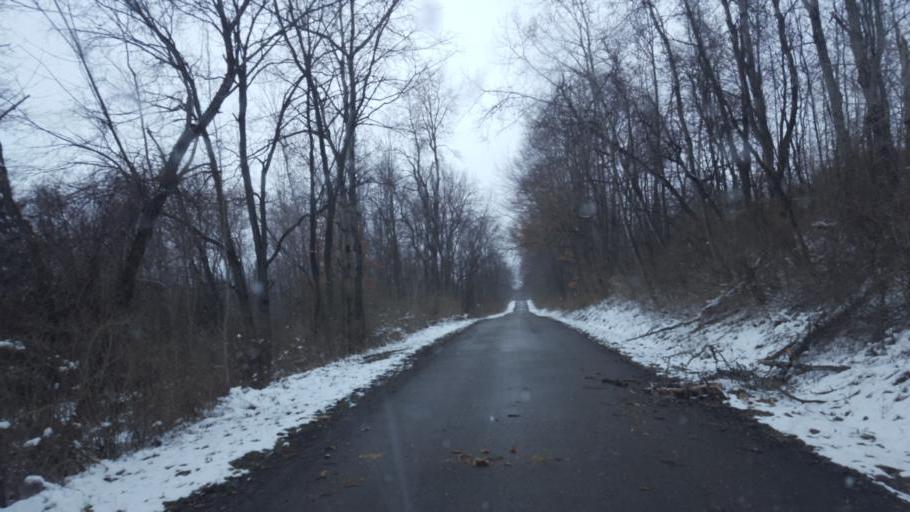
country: US
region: Pennsylvania
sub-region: Mercer County
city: Stoneboro
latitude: 41.3891
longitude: -80.0902
